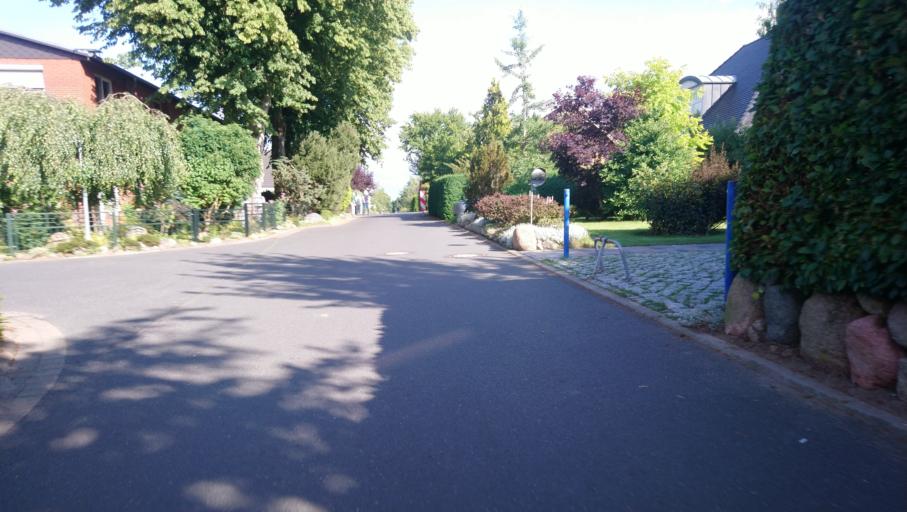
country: DE
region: Mecklenburg-Vorpommern
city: Papendorf
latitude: 54.0595
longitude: 12.1095
